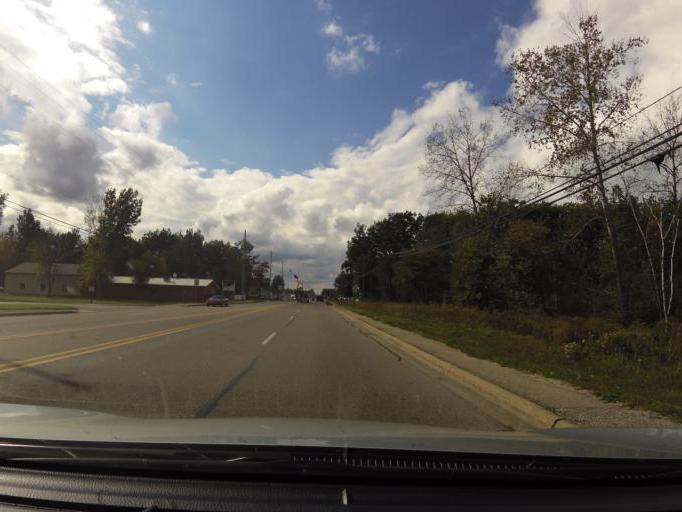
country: US
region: Michigan
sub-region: Roscommon County
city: Prudenville
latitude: 44.2987
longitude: -84.6838
